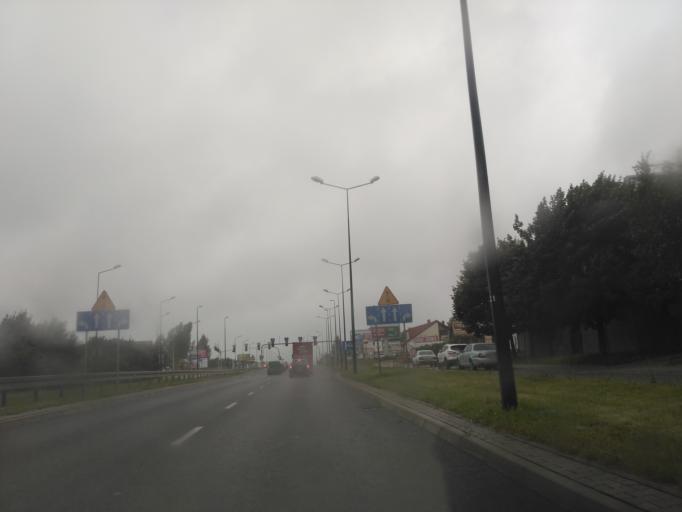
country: PL
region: Lublin Voivodeship
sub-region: Powiat lubelski
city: Lublin
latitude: 51.2740
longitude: 22.5737
